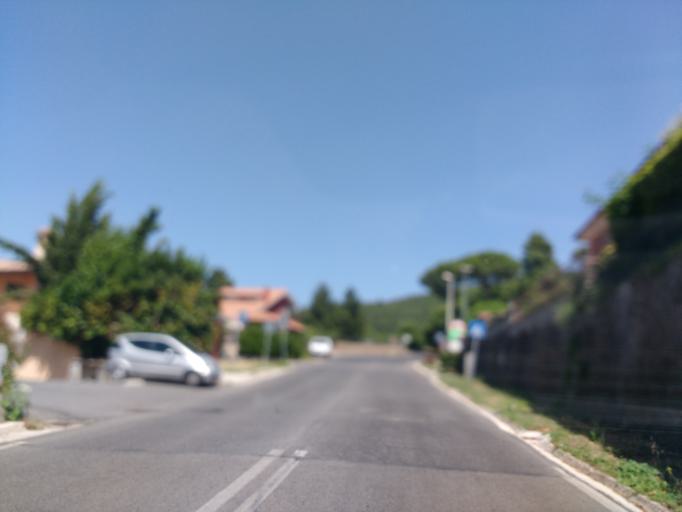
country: IT
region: Latium
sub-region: Citta metropolitana di Roma Capitale
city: Rocca di Papa
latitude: 41.7672
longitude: 12.7104
